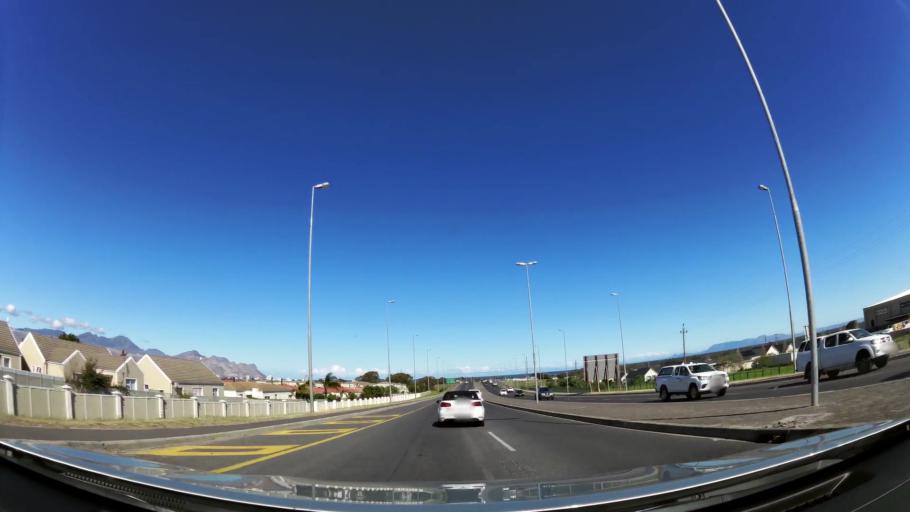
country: ZA
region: Western Cape
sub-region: Cape Winelands District Municipality
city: Stellenbosch
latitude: -34.0716
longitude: 18.8244
